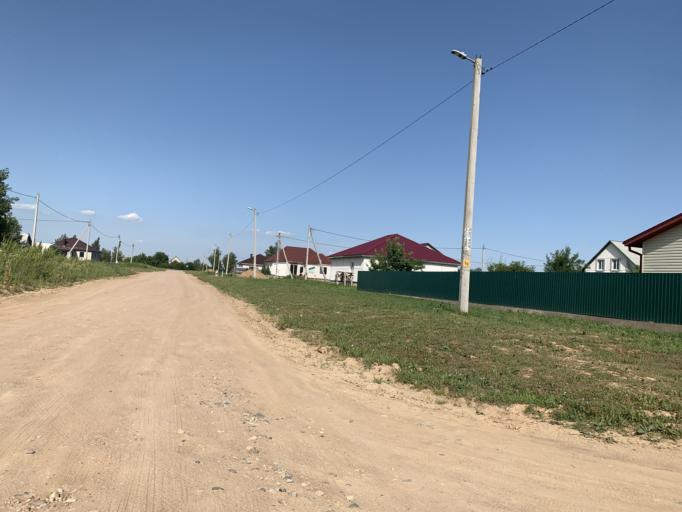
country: BY
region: Minsk
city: Dzyarzhynsk
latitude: 53.7015
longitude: 27.0901
